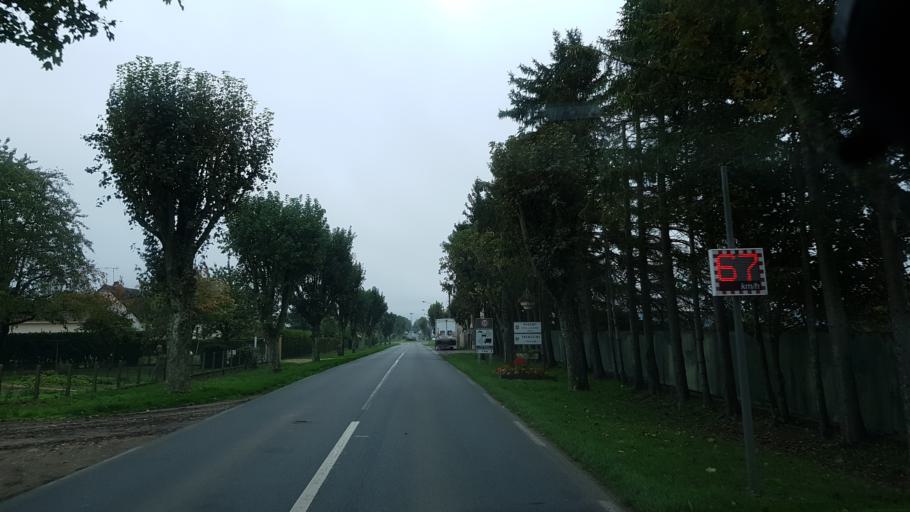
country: FR
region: Ile-de-France
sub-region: Departement de l'Essonne
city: Pussay
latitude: 48.3541
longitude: 1.9852
